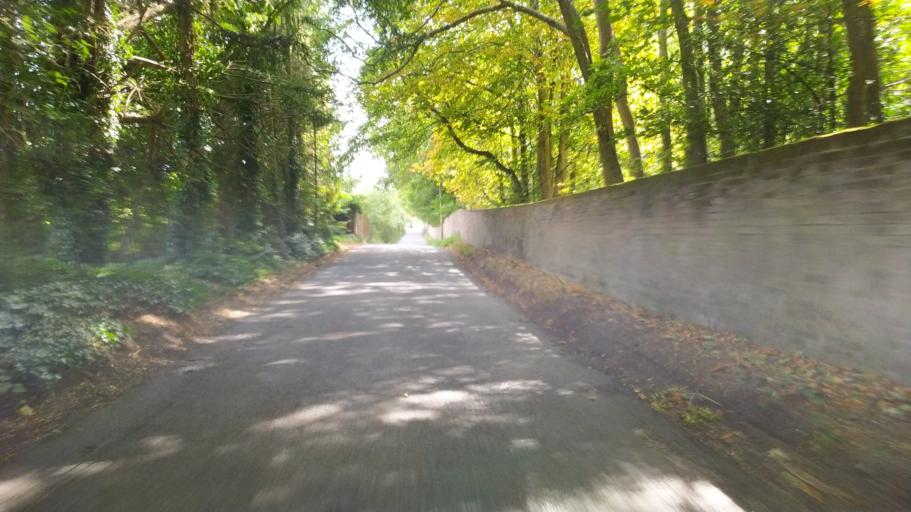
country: GB
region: England
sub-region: Dorset
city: Blandford Forum
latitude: 50.8482
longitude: -2.1379
